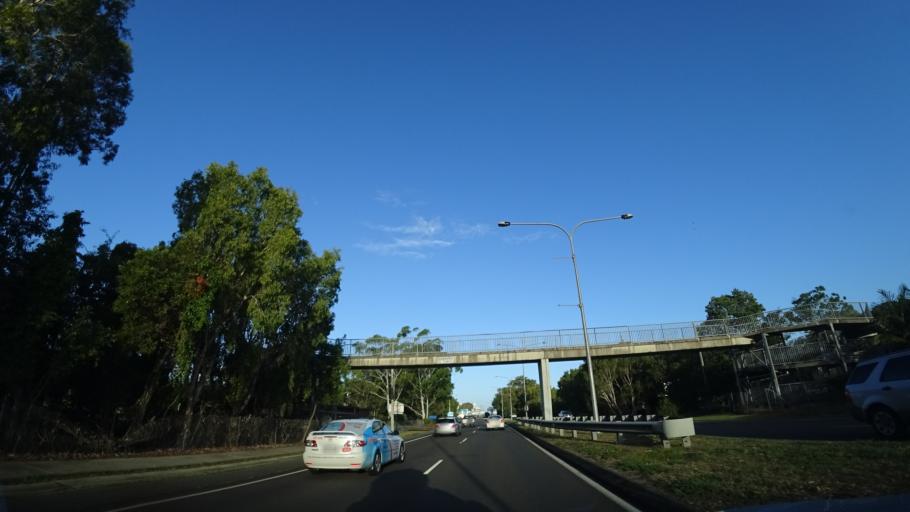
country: AU
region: Queensland
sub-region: Sunshine Coast
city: Buderim
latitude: -26.6521
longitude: 153.0839
